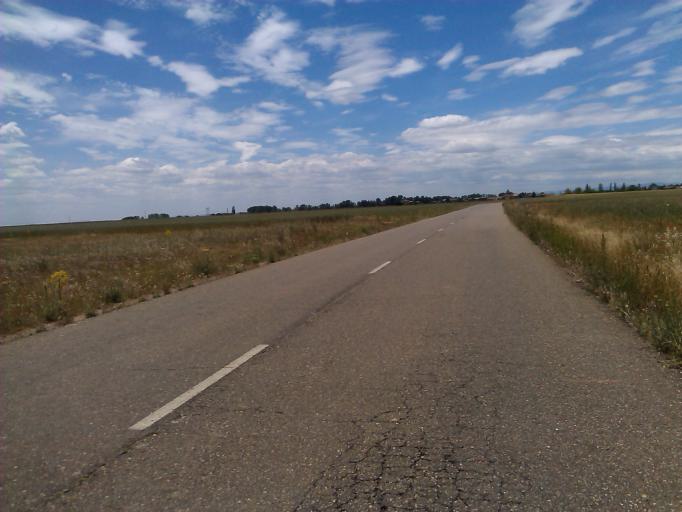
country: ES
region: Castille and Leon
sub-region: Provincia de Leon
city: Chozas de Abajo
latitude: 42.4889
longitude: -5.7161
